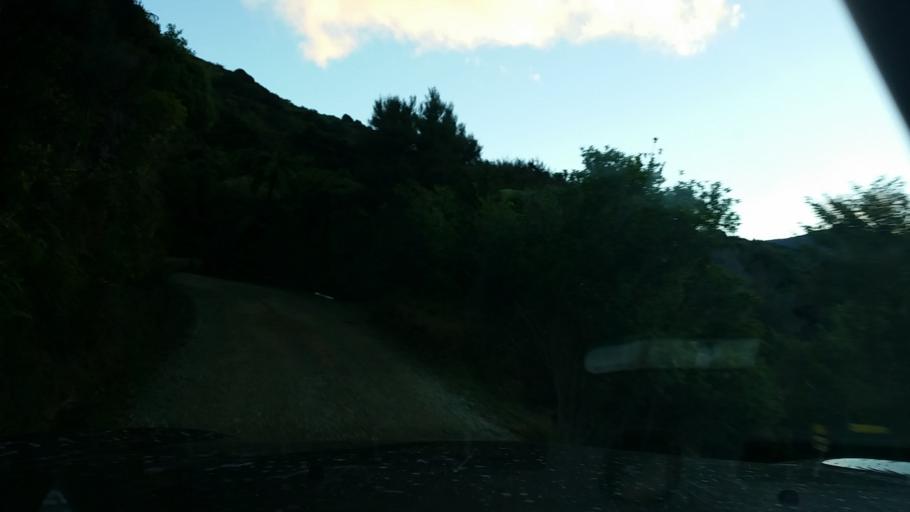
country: NZ
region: Marlborough
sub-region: Marlborough District
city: Picton
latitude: -41.1310
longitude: 174.1480
